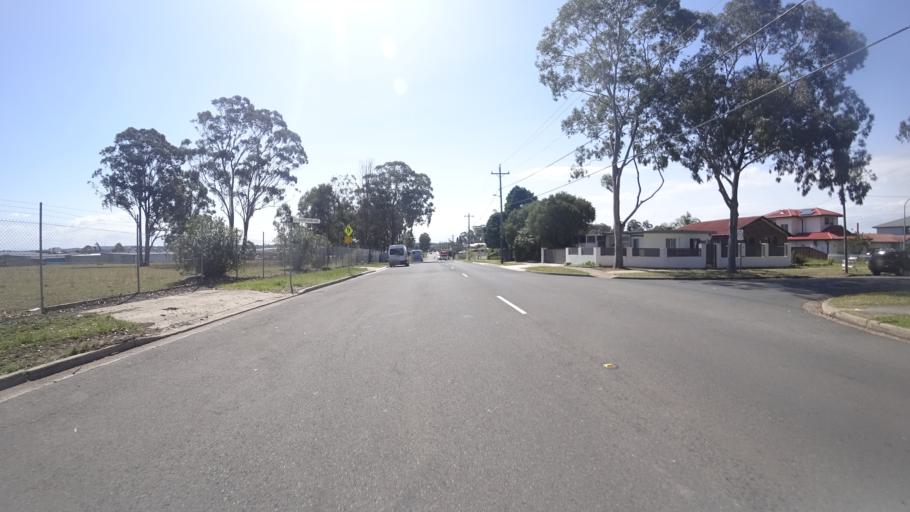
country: AU
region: New South Wales
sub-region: Liverpool
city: Miller
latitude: -33.9415
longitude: 150.8889
